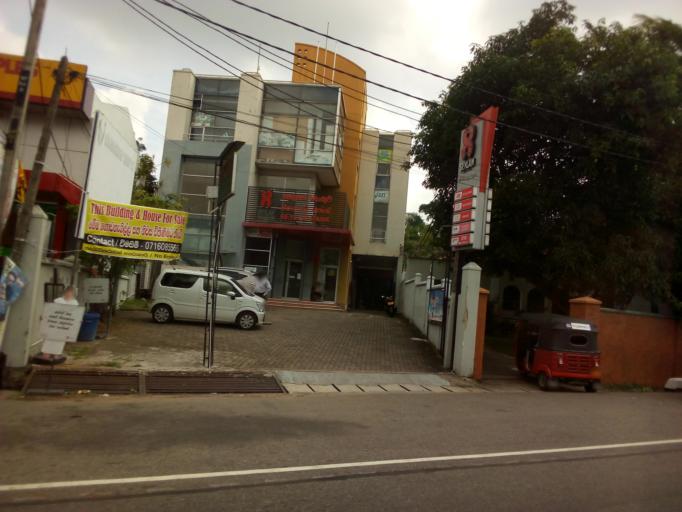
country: LK
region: Western
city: Maharagama
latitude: 6.8585
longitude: 79.9076
